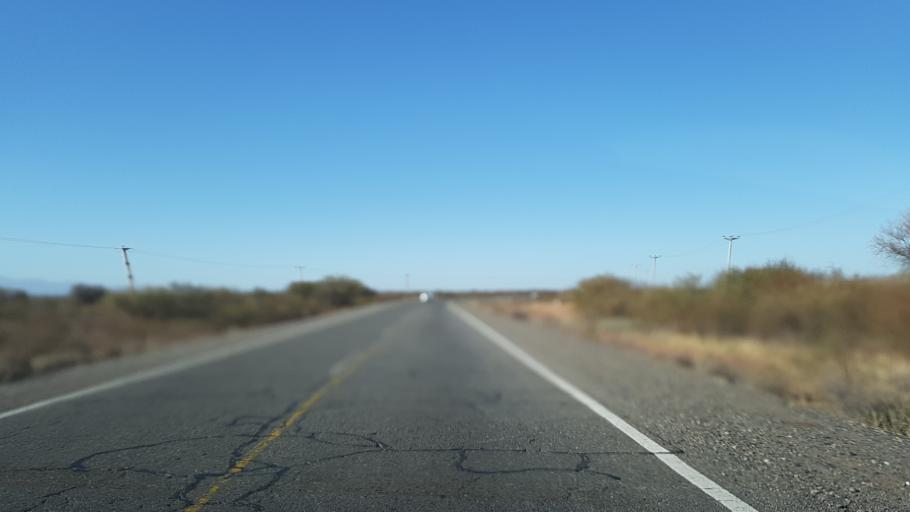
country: AR
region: San Juan
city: Caucete
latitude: -31.5985
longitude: -67.6965
